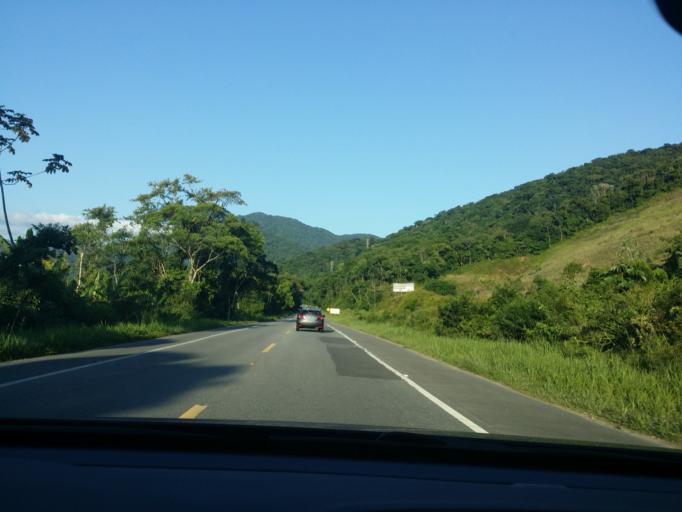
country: BR
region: Sao Paulo
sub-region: Sao Sebastiao
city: Sao Sebastiao
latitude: -23.7492
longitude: -45.7452
